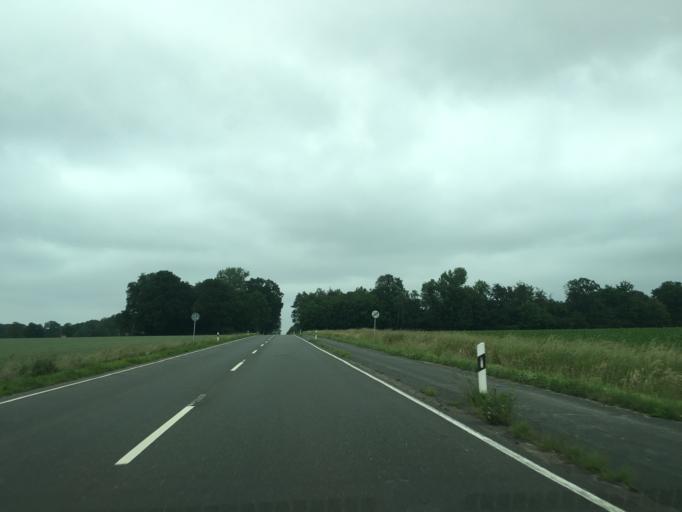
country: DE
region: North Rhine-Westphalia
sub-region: Regierungsbezirk Munster
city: Steinfurt
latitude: 52.1236
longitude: 7.3380
